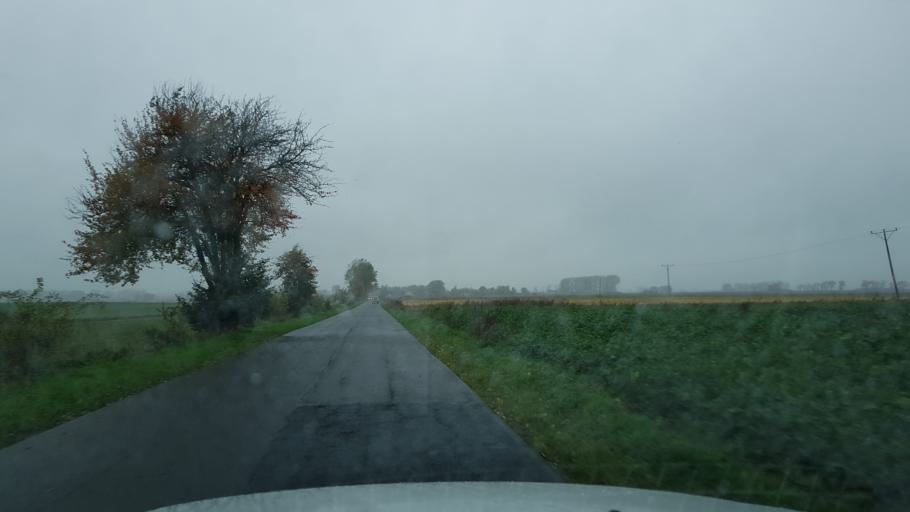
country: PL
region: West Pomeranian Voivodeship
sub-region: Powiat pyrzycki
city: Pyrzyce
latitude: 53.1581
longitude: 14.8608
